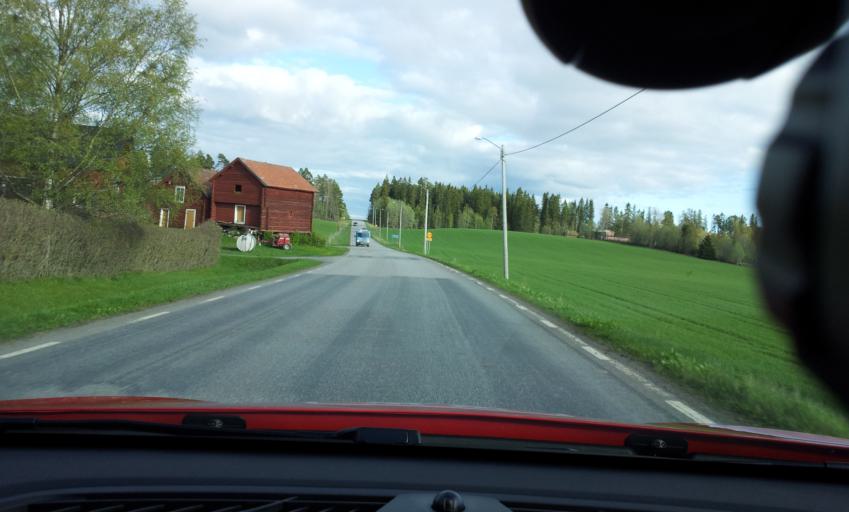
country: SE
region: Jaemtland
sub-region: Krokoms Kommun
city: Krokom
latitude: 63.2533
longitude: 14.4113
